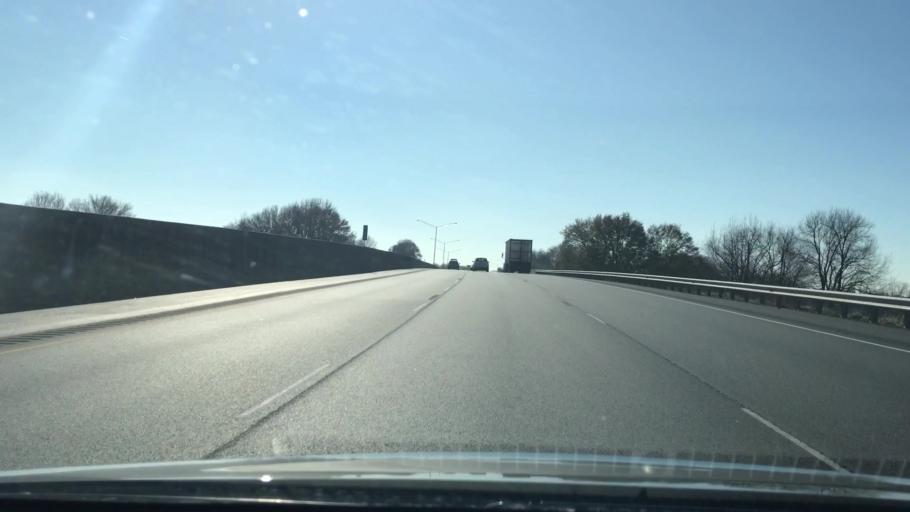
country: US
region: Kentucky
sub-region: Edmonson County
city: Brownsville
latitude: 37.0306
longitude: -86.2385
